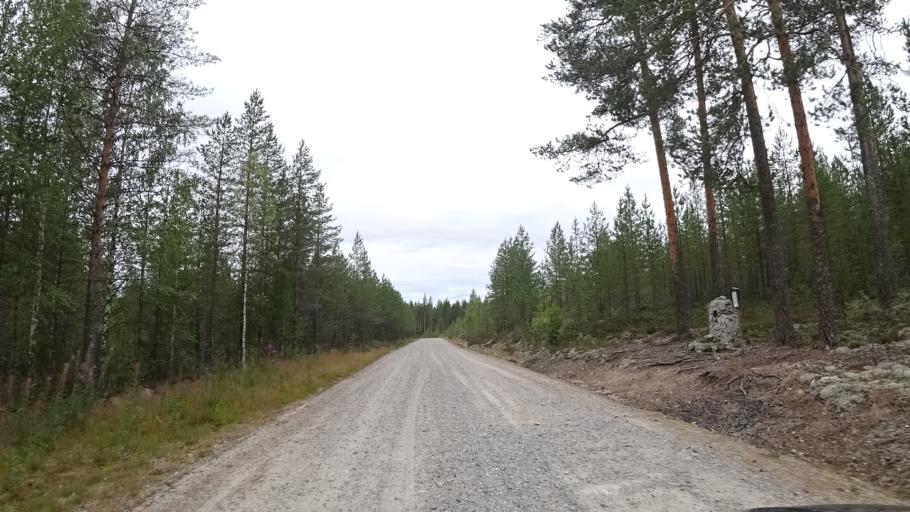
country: FI
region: North Karelia
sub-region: Joensuu
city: Ilomantsi
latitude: 63.1545
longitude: 30.6379
